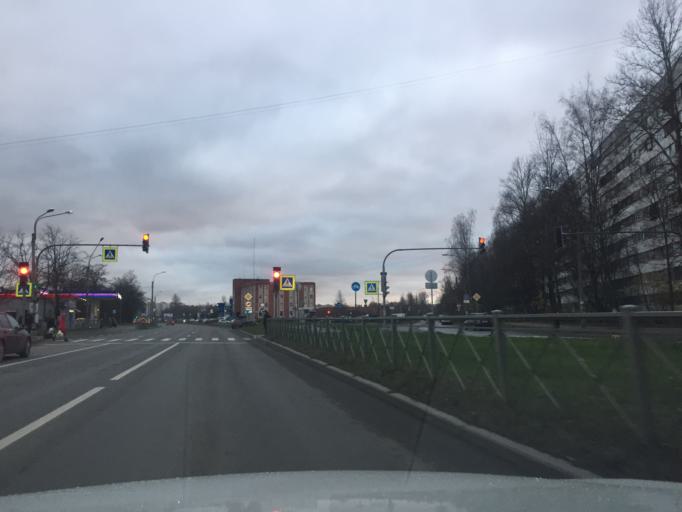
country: RU
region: St.-Petersburg
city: Grazhdanka
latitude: 60.0273
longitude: 30.4313
